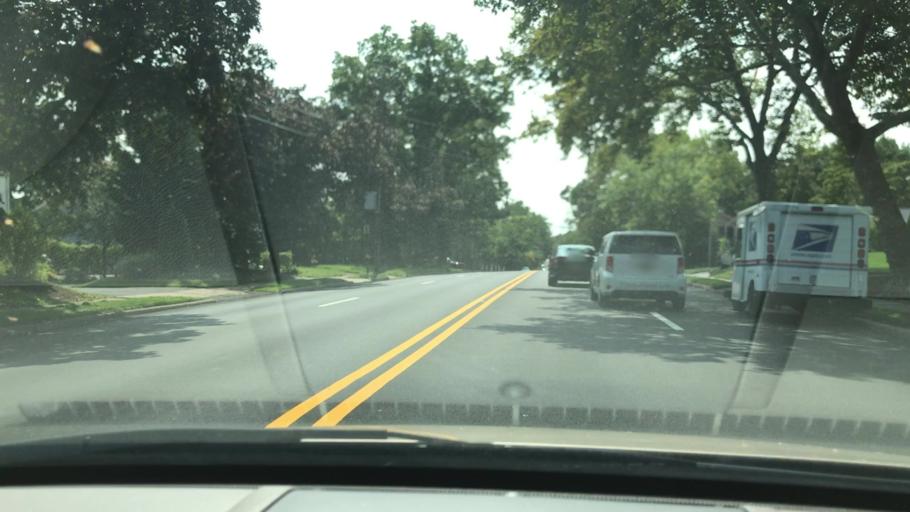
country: US
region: New Jersey
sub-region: Bergen County
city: Oradell
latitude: 40.9547
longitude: -74.0512
